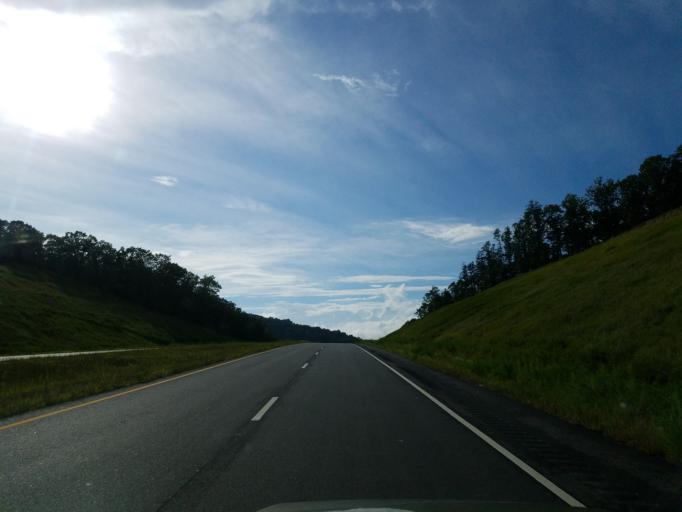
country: US
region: Georgia
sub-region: White County
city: Cleveland
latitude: 34.5809
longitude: -83.7672
